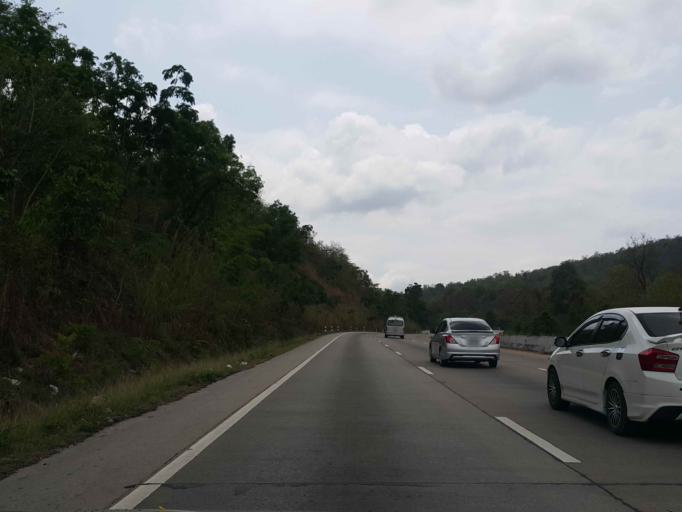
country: TH
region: Lamphun
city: Mae Tha
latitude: 18.4373
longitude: 99.2055
